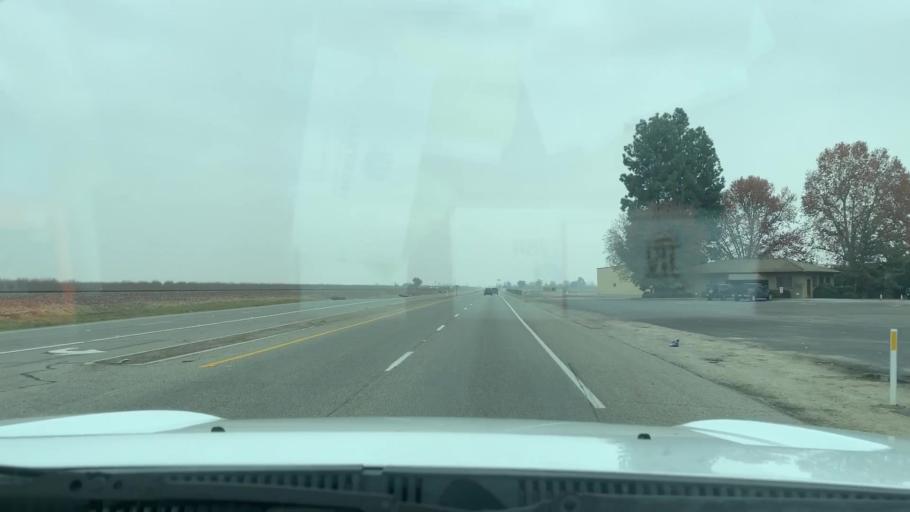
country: US
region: California
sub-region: Kern County
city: Shafter
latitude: 35.5275
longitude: -119.3043
